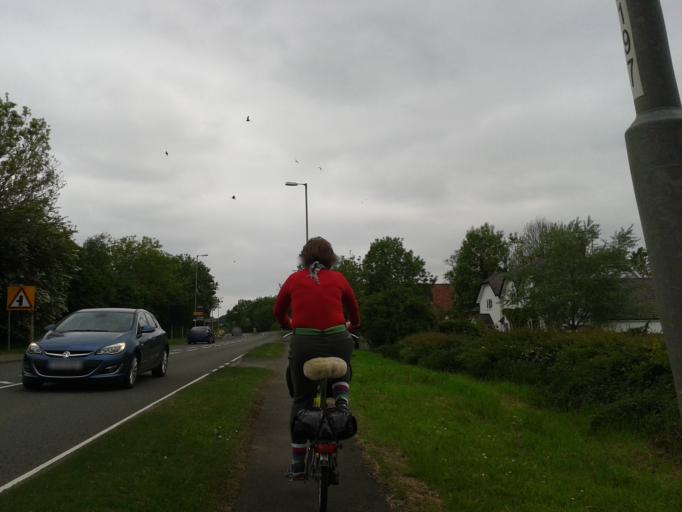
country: GB
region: England
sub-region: Leicestershire
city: Kibworth Harcourt
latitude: 52.5371
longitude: -0.9824
